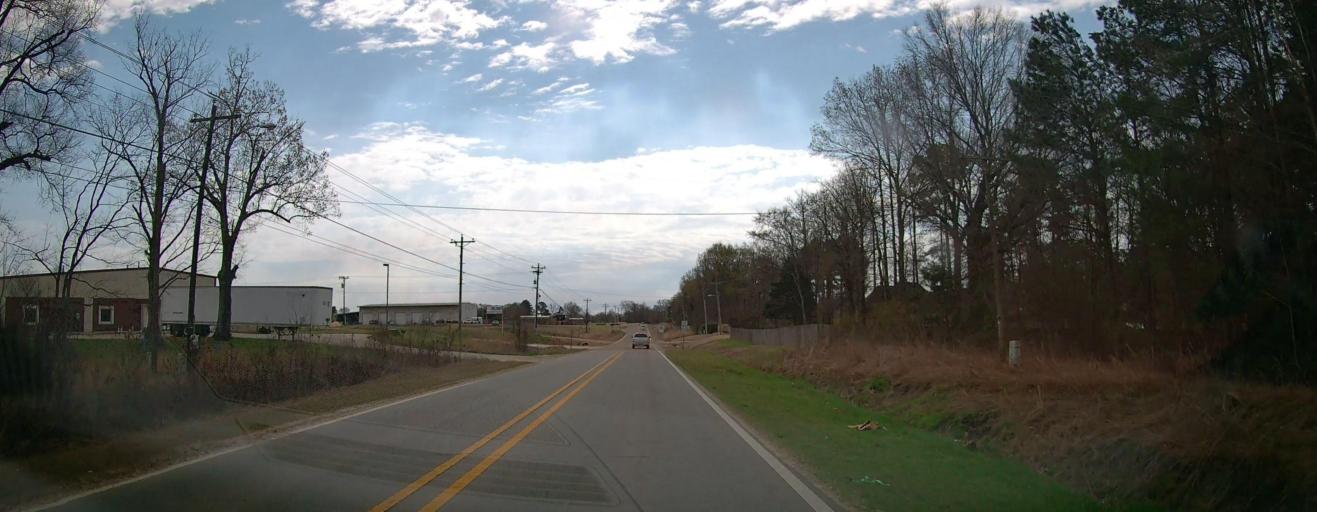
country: US
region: Mississippi
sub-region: De Soto County
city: Olive Branch
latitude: 34.9448
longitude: -89.8081
